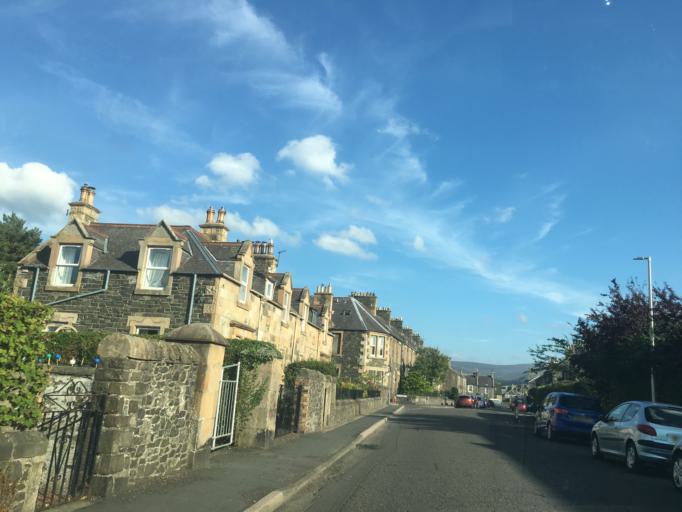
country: GB
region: Scotland
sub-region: The Scottish Borders
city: Peebles
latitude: 55.6545
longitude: -3.1941
